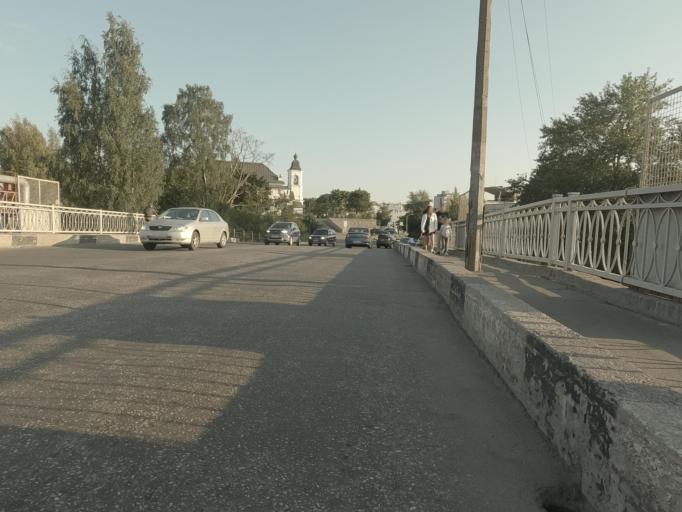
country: RU
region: Leningrad
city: Vyborg
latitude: 60.7151
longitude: 28.7577
